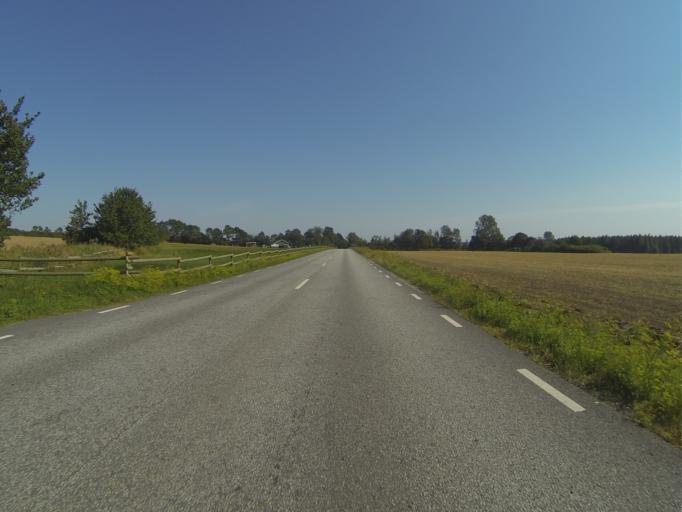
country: SE
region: Skane
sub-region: Hoors Kommun
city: Loberod
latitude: 55.7083
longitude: 13.5557
